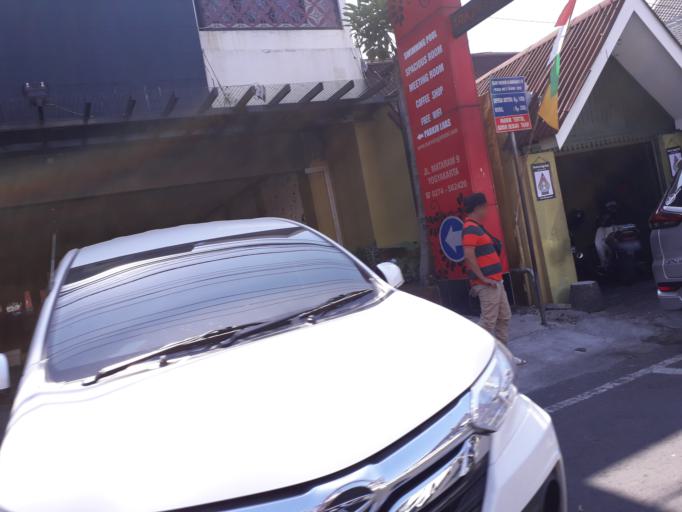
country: ID
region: Daerah Istimewa Yogyakarta
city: Yogyakarta
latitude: -7.7960
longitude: 110.3691
